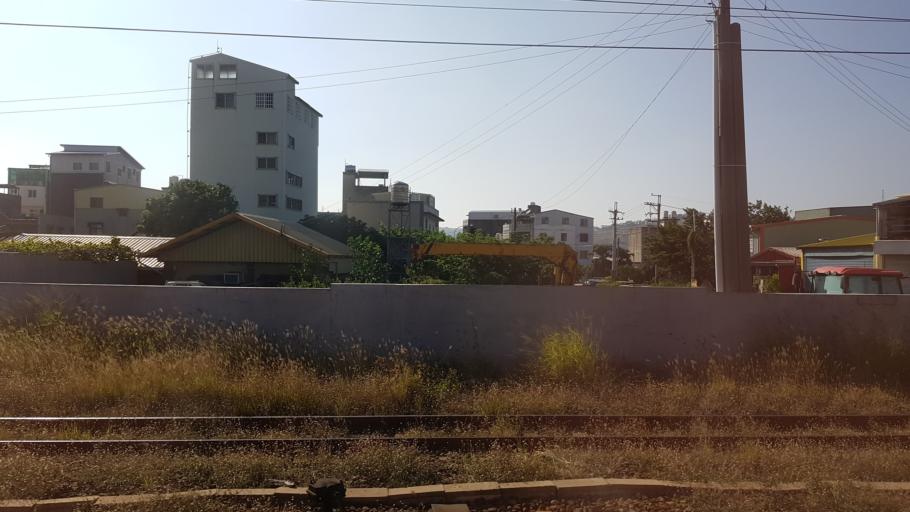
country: TW
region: Taiwan
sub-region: Miaoli
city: Miaoli
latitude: 24.5726
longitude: 120.8217
